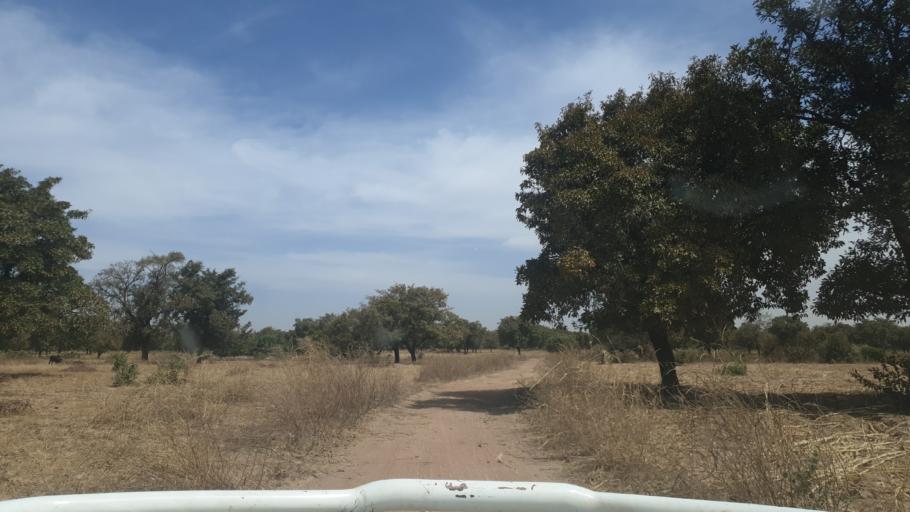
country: ML
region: Sikasso
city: Yorosso
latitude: 12.2860
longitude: -4.6797
